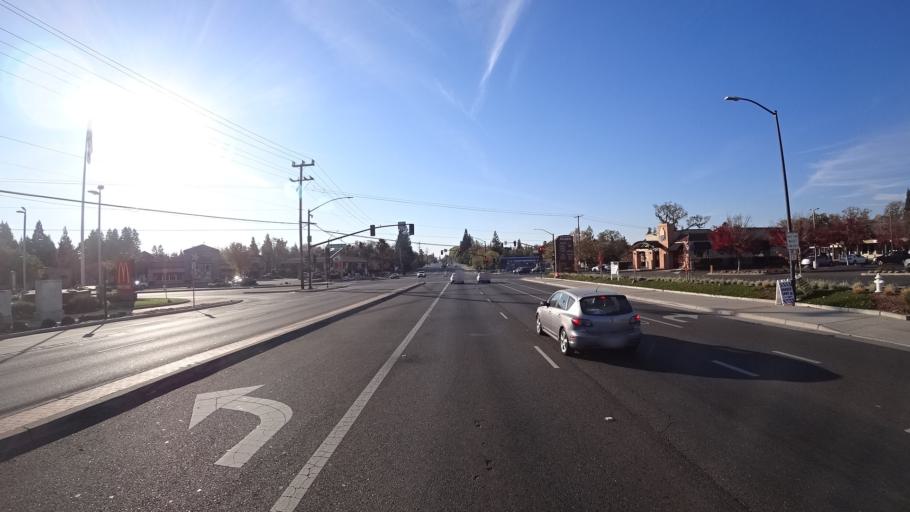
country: US
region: California
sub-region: Sacramento County
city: Citrus Heights
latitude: 38.7045
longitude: -121.2719
